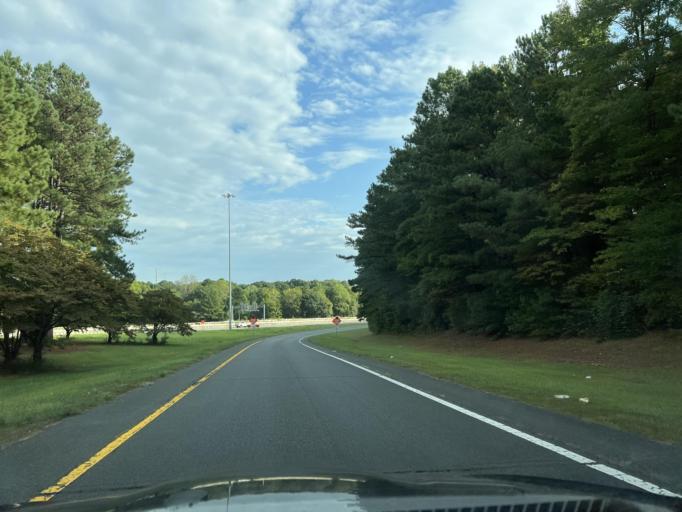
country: US
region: North Carolina
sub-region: Wake County
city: Cary
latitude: 35.7661
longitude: -78.7326
